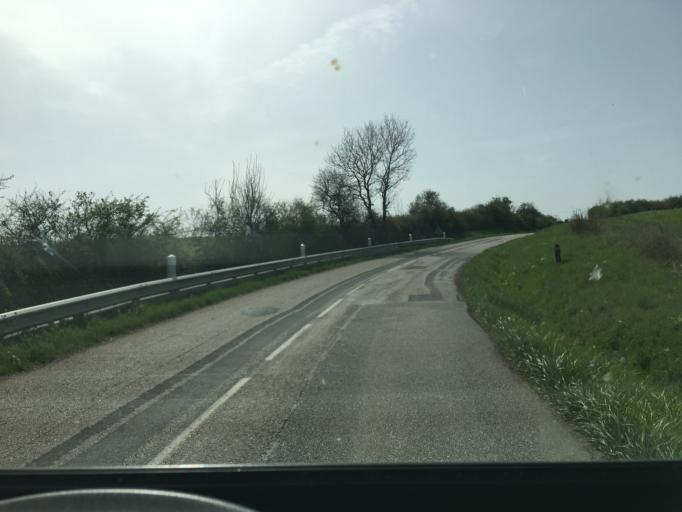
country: FR
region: Lorraine
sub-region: Departement de Meurthe-et-Moselle
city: Fleville-devant-Nancy
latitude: 48.6204
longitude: 6.2281
